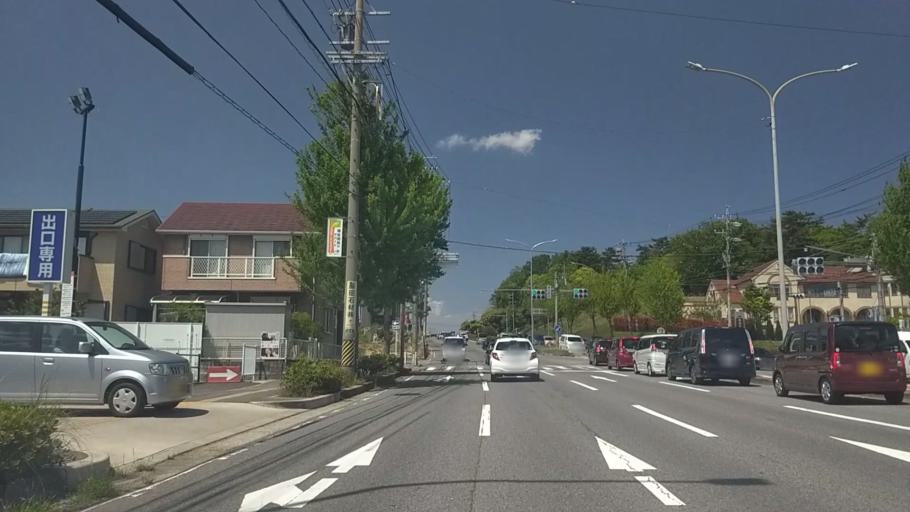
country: JP
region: Aichi
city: Okazaki
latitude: 34.9518
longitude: 137.1898
